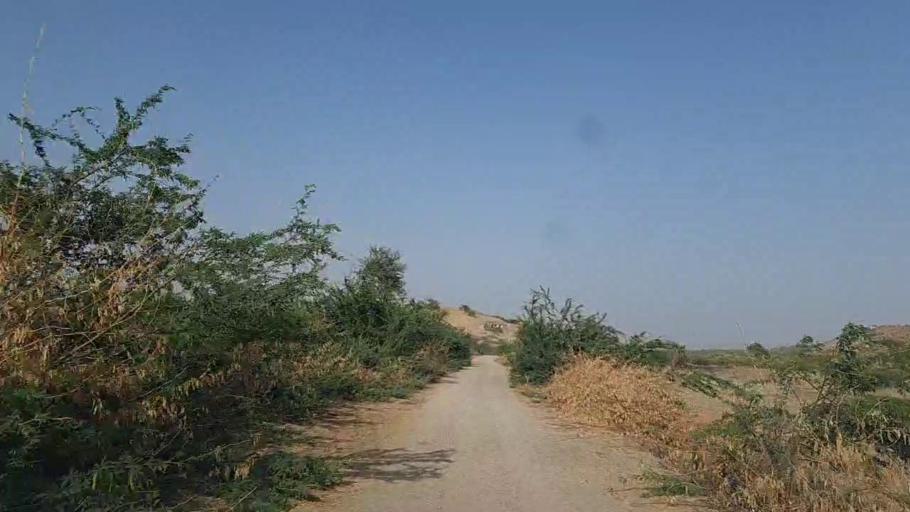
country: PK
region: Sindh
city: Naukot
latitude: 24.5955
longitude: 69.3145
